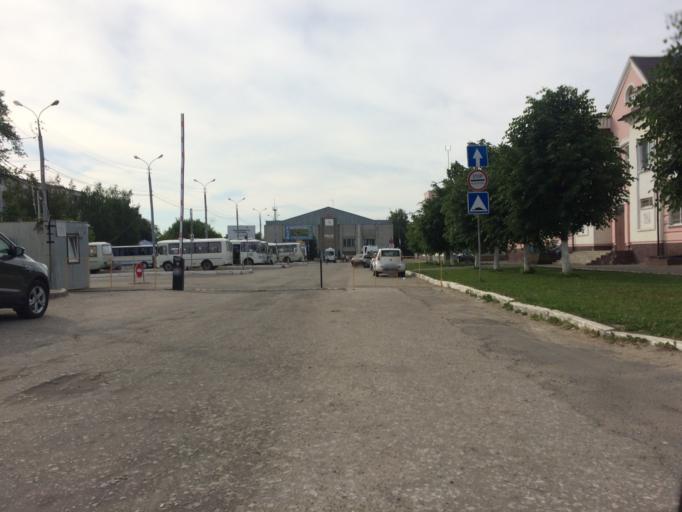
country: RU
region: Mariy-El
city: Yoshkar-Ola
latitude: 56.6216
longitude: 47.8811
